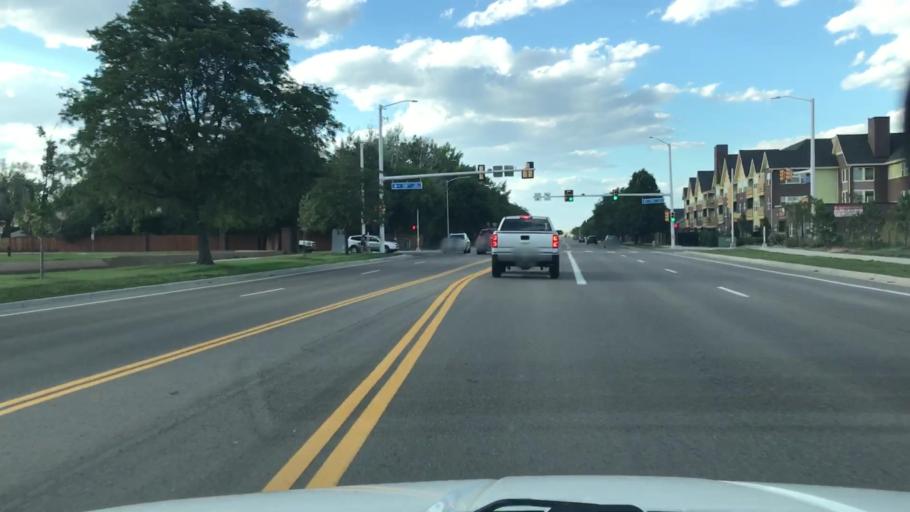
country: US
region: Colorado
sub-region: Broomfield County
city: Broomfield
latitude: 39.9207
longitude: -105.0344
